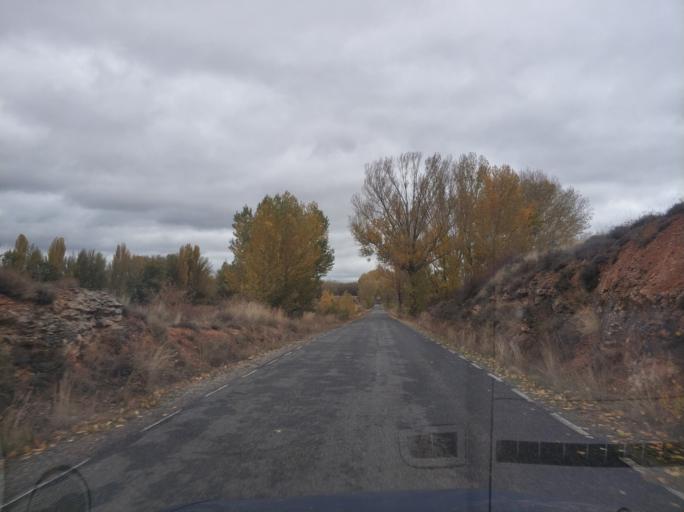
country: ES
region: Castille and Leon
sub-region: Provincia de Soria
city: San Esteban de Gormaz
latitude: 41.5826
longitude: -3.1991
